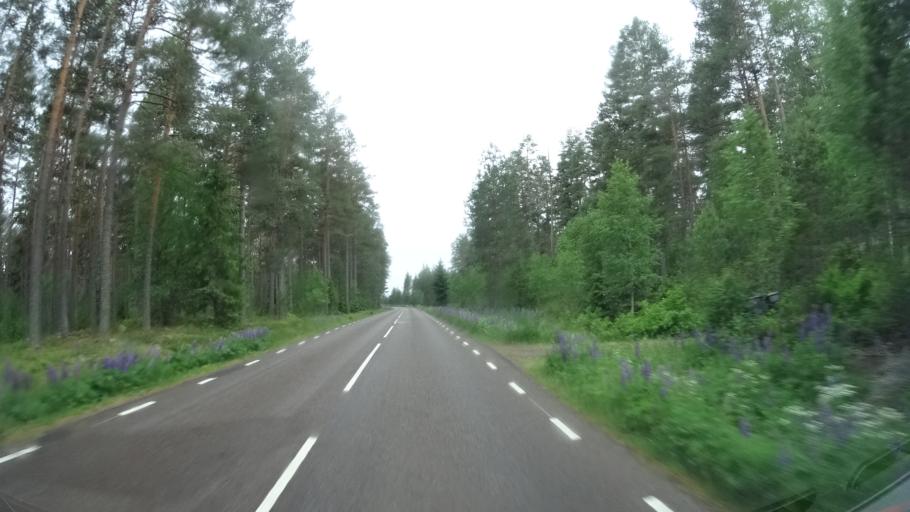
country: SE
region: Joenkoeping
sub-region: Eksjo Kommun
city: Mariannelund
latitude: 57.6342
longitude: 15.6025
